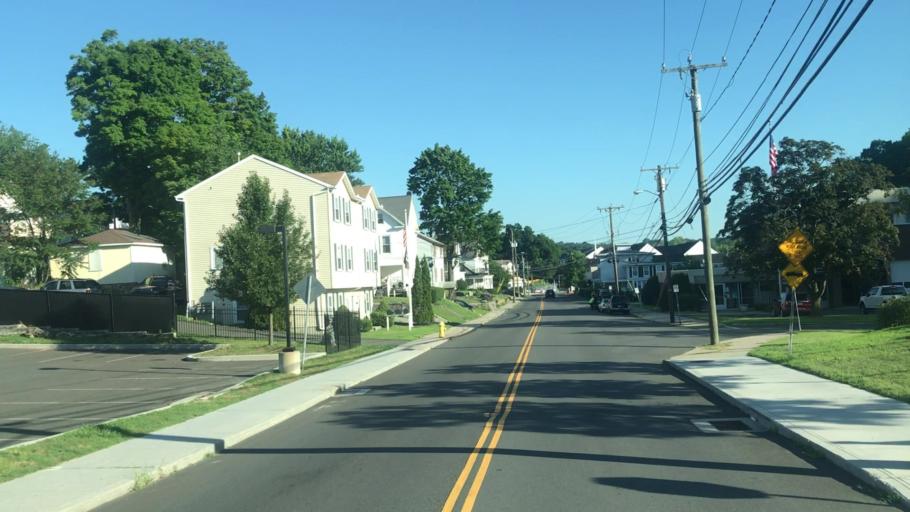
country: US
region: Connecticut
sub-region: Fairfield County
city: Danbury
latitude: 41.3930
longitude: -73.4552
